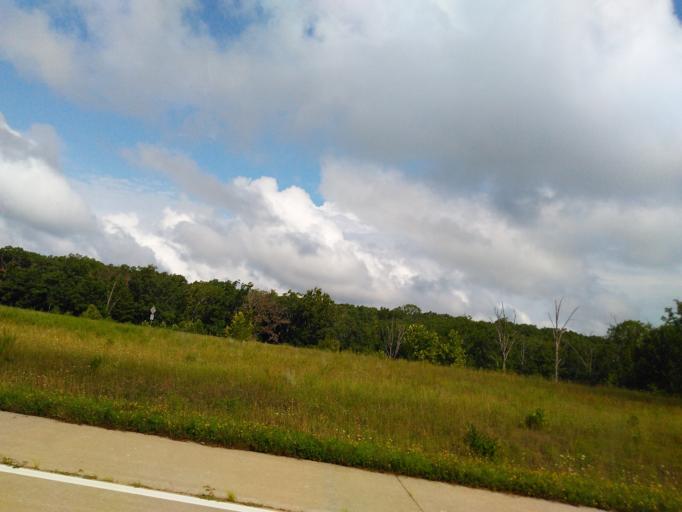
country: US
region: Missouri
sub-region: Jefferson County
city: Hillsboro
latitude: 38.2524
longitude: -90.5585
